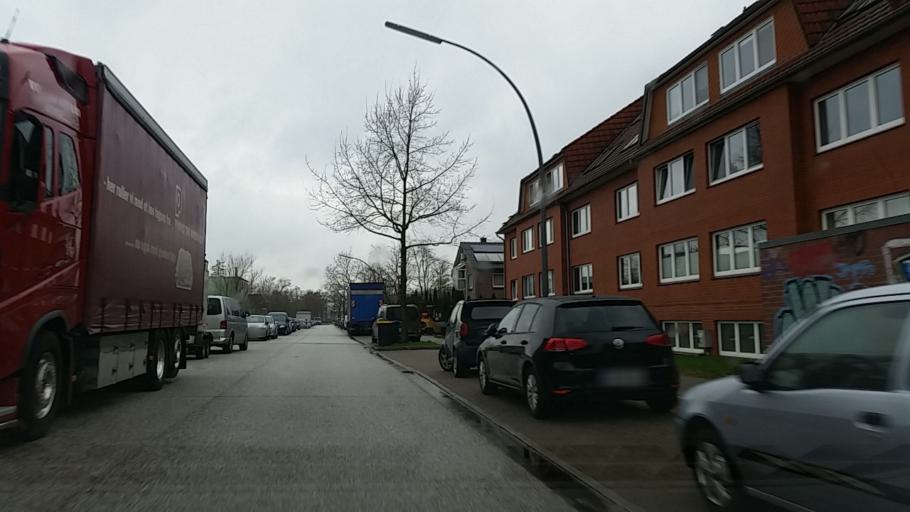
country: DE
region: Hamburg
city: Bergedorf
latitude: 53.4805
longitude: 10.2230
